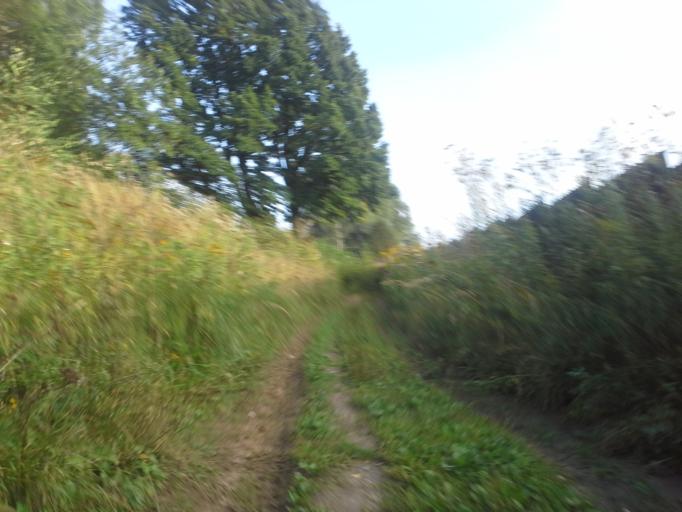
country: RU
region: Moskovskaya
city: Filimonki
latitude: 55.5474
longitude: 37.3376
